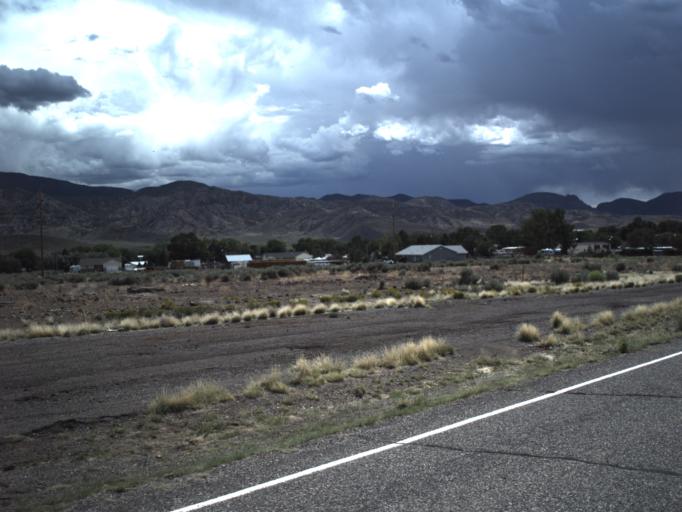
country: US
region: Utah
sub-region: Piute County
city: Junction
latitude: 38.2410
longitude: -112.2298
